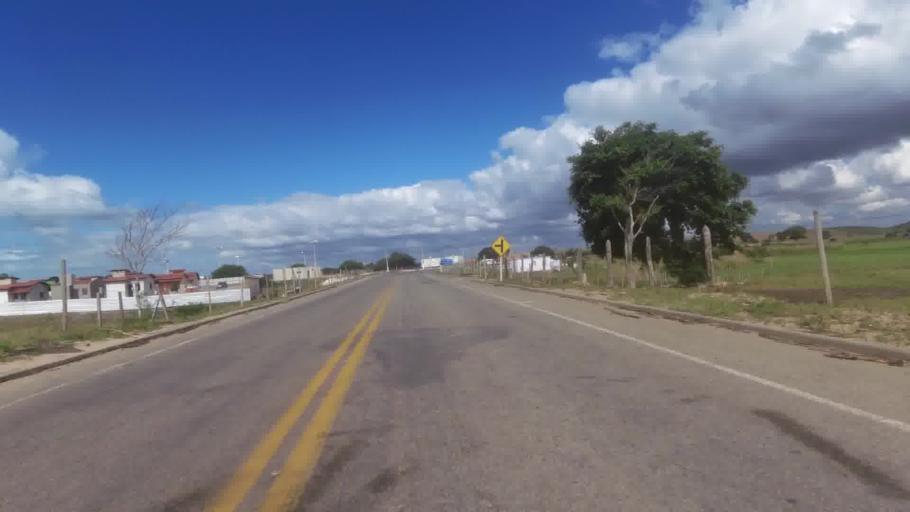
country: BR
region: Espirito Santo
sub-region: Marataizes
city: Marataizes
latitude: -21.1862
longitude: -40.9327
